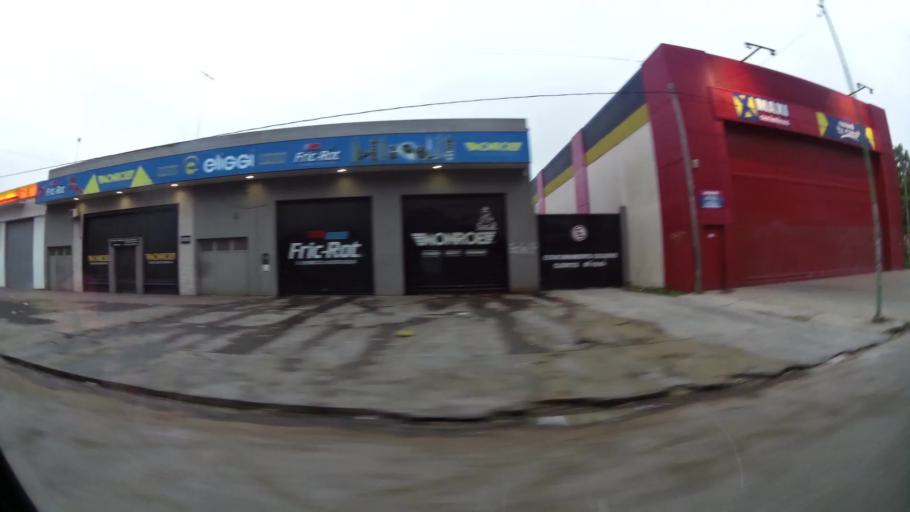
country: AR
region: Buenos Aires
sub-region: Partido de La Plata
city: La Plata
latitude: -34.9090
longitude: -57.9791
